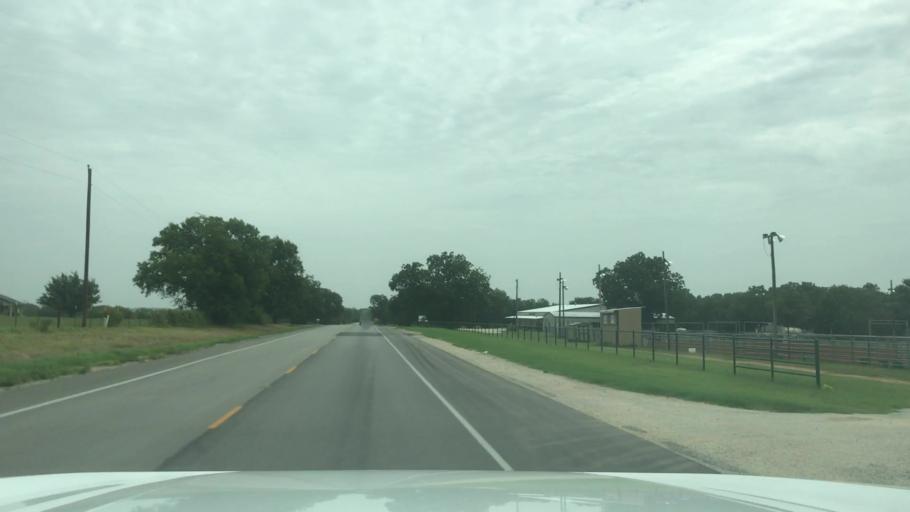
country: US
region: Texas
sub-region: Erath County
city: Dublin
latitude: 32.0909
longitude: -98.2782
